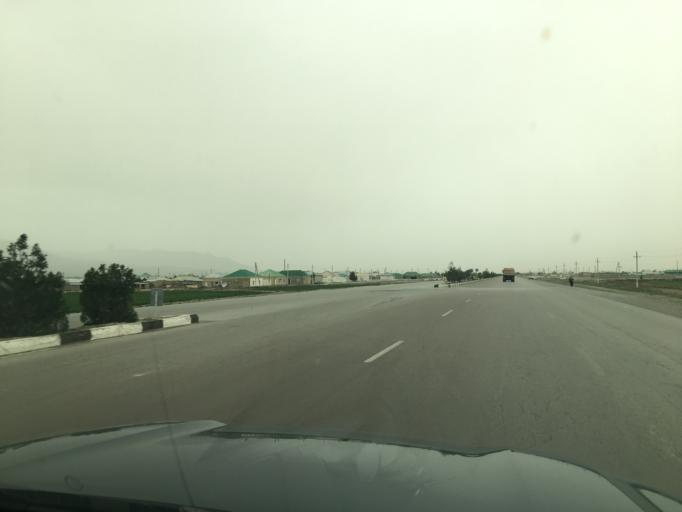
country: TM
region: Ahal
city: Baharly
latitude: 38.3932
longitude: 57.4827
